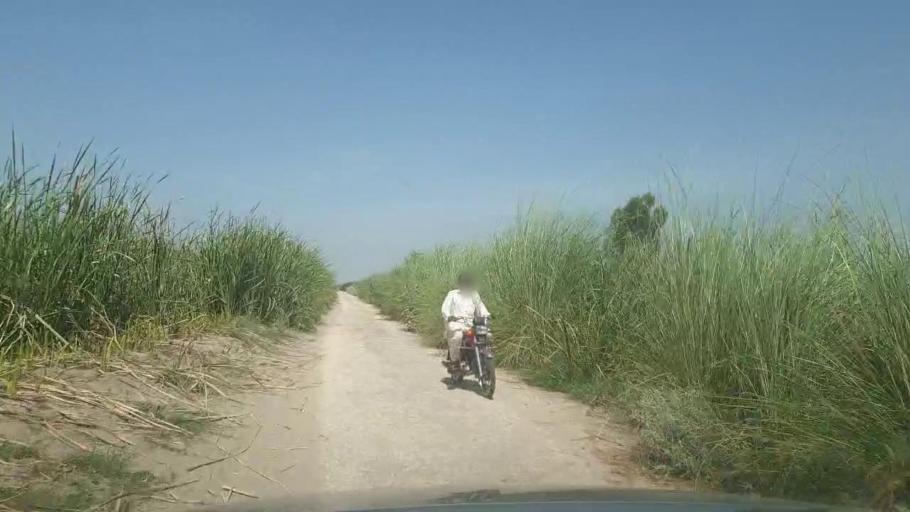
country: PK
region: Sindh
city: Khairpur
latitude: 27.3987
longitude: 69.0607
